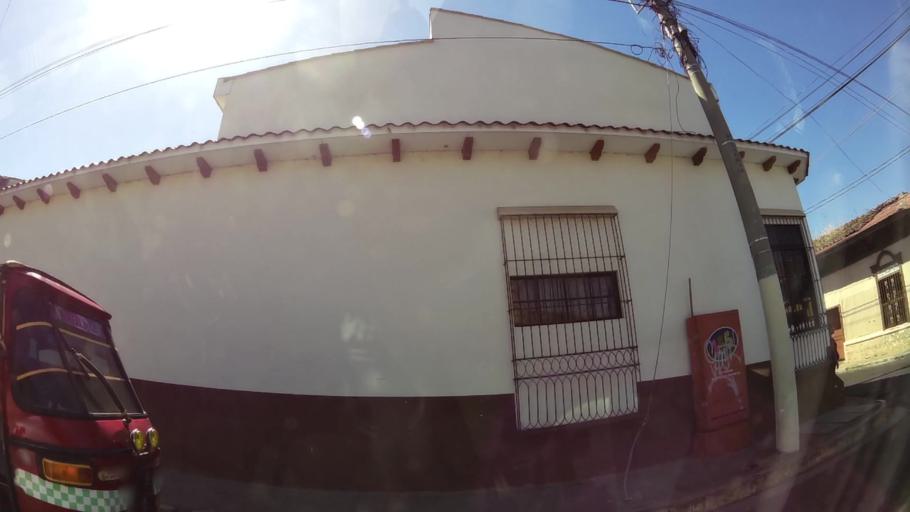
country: SV
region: Ahuachapan
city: Ahuachapan
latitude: 13.9195
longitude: -89.8457
